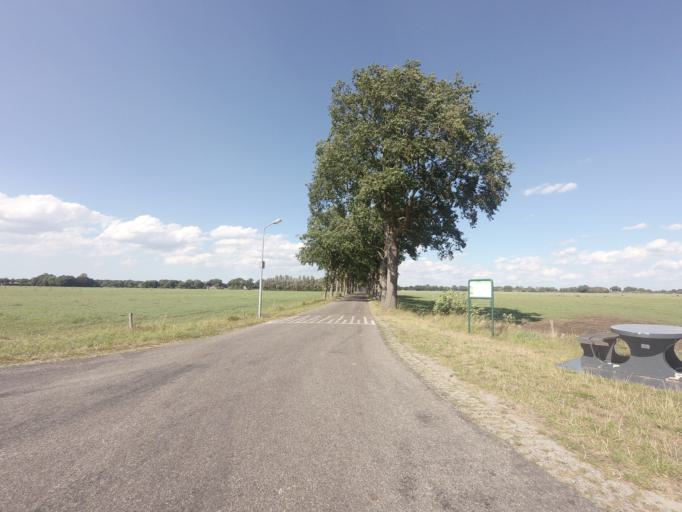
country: NL
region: Drenthe
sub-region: Gemeente Hoogeveen
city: Hoogeveen
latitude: 52.6255
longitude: 6.4825
